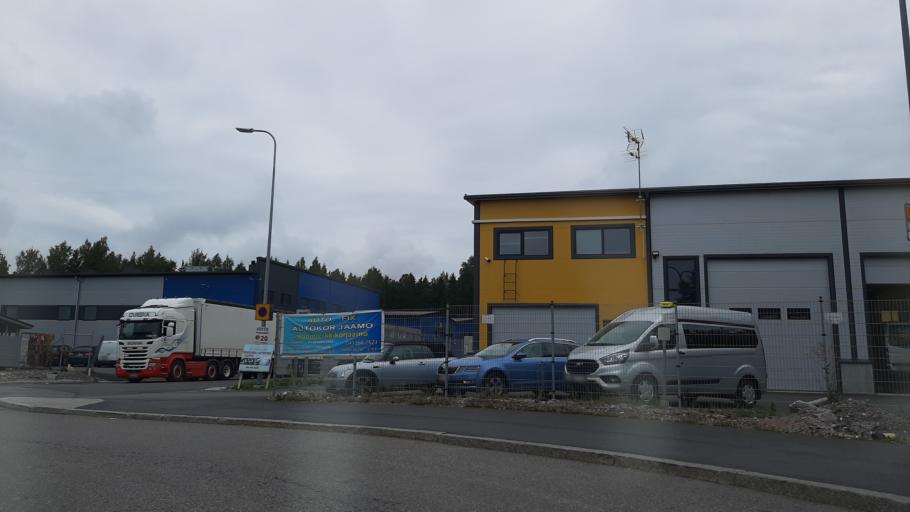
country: FI
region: Uusimaa
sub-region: Helsinki
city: Vantaa
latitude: 60.2460
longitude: 25.0622
